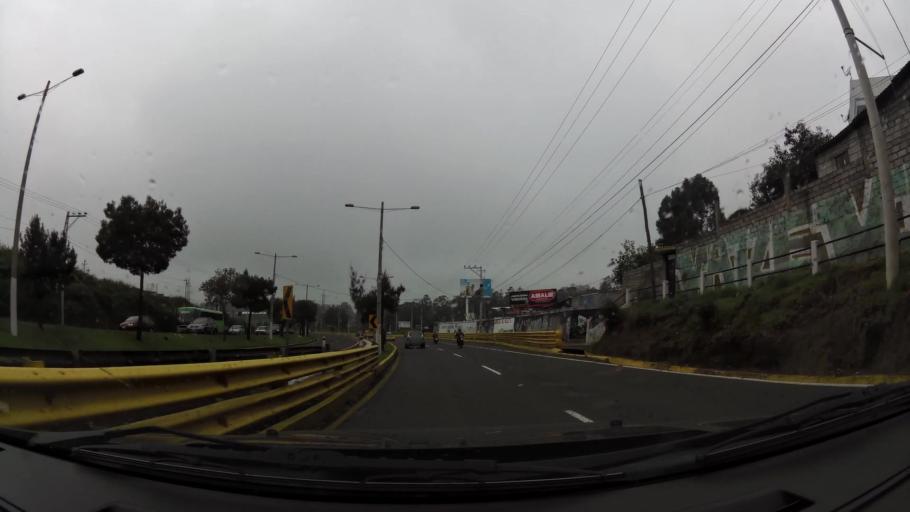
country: EC
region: Pichincha
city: Quito
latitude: -0.2744
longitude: -78.4905
